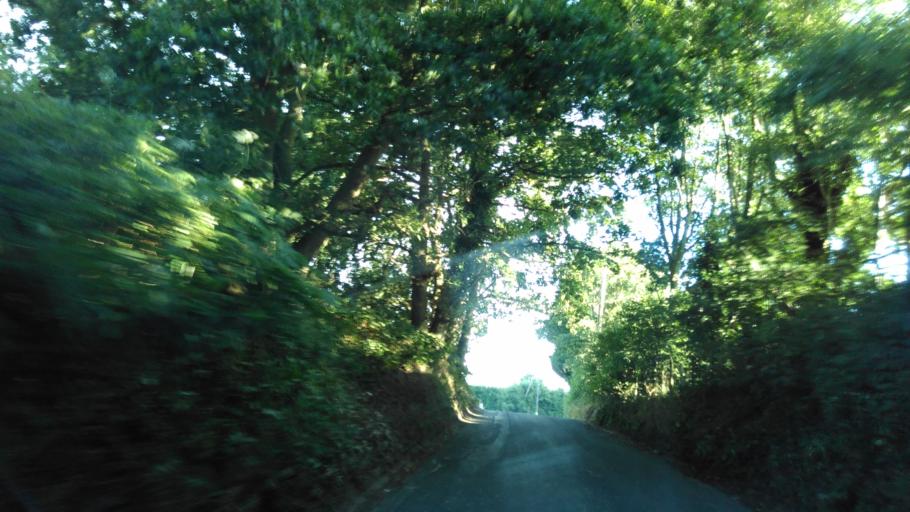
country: GB
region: England
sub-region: Kent
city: Chartham
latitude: 51.2794
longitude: 1.0090
